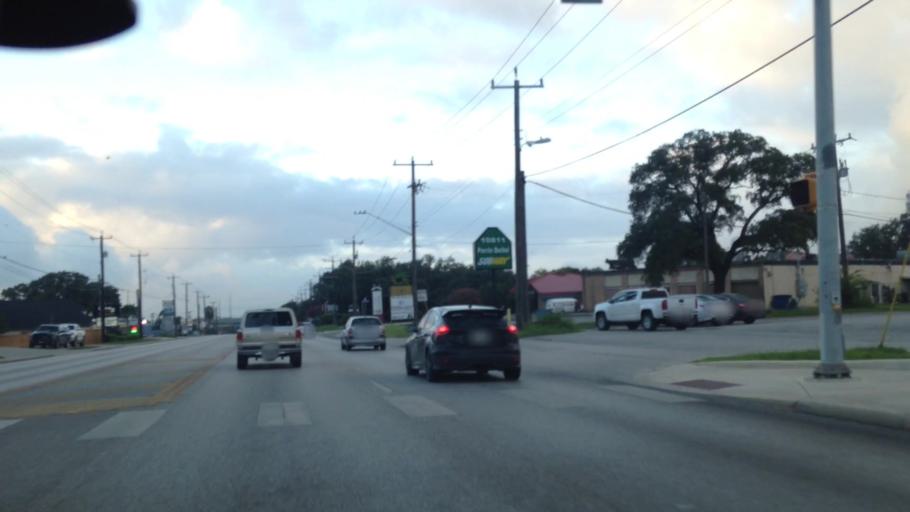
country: US
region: Texas
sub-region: Bexar County
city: Windcrest
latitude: 29.5398
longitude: -98.4111
